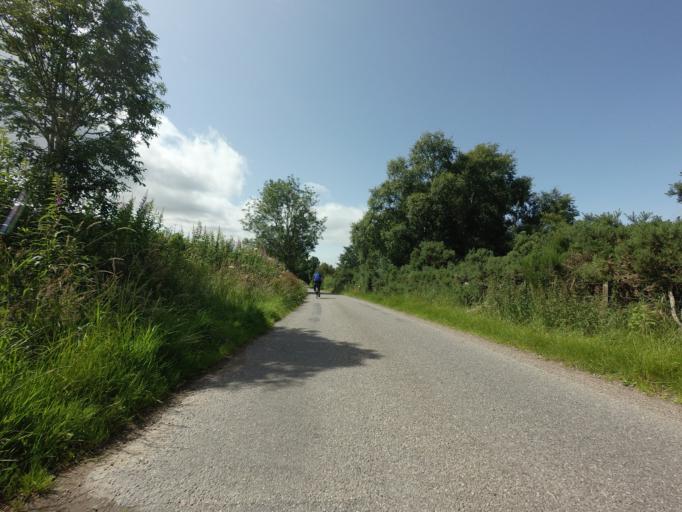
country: GB
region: Scotland
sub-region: Highland
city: Fortrose
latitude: 57.4903
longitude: -4.0175
